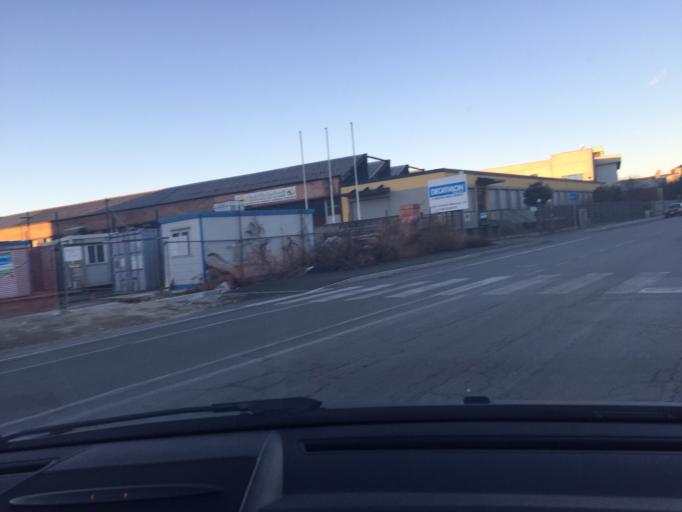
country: IT
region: Piedmont
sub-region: Provincia di Torino
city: Grugliasco
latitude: 45.0589
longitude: 7.5874
